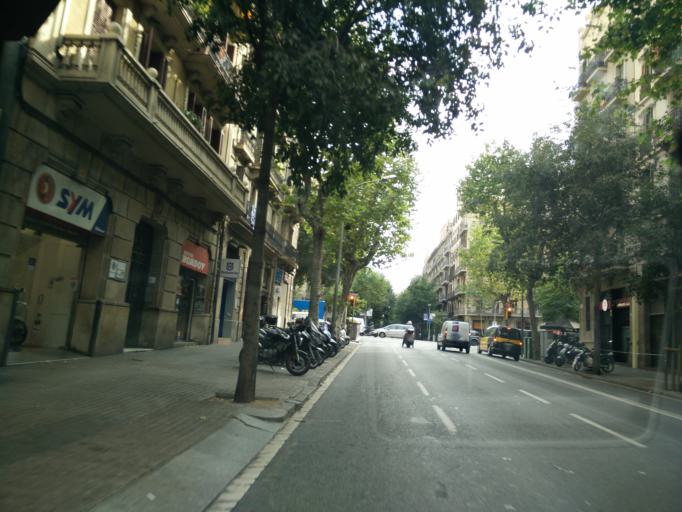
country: ES
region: Catalonia
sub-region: Provincia de Barcelona
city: Barcelona
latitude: 41.3885
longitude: 2.1579
